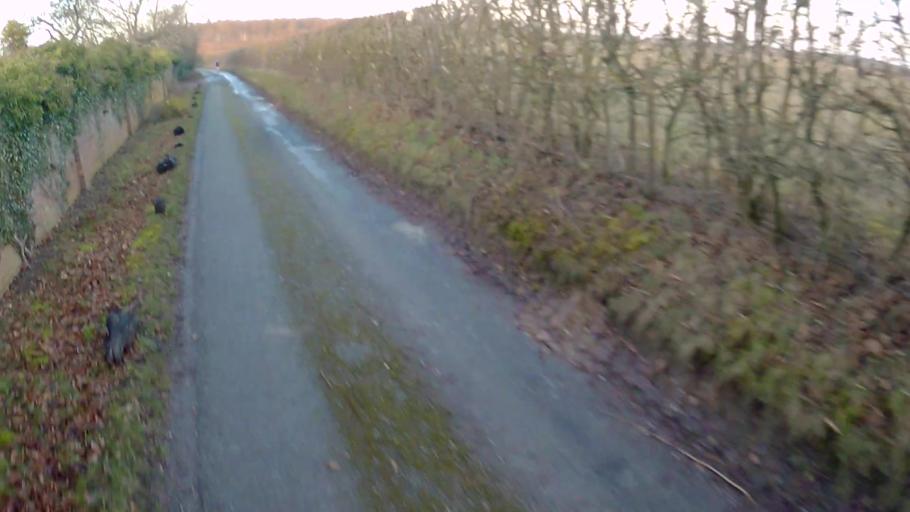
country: GB
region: England
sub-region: Hampshire
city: Overton
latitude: 51.2178
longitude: -1.2440
